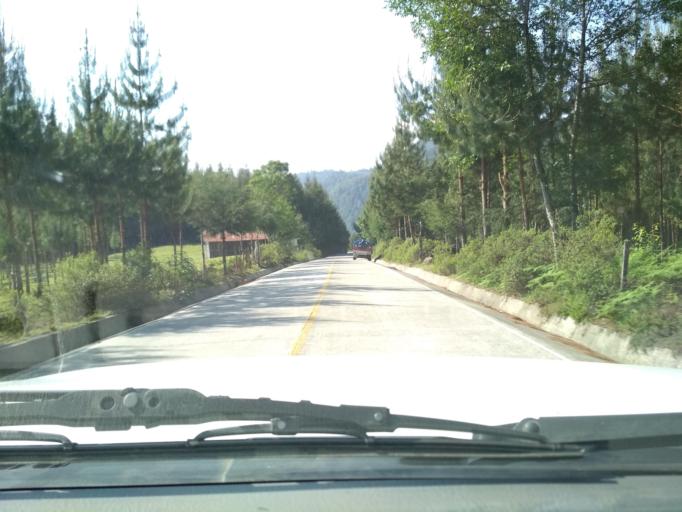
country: MX
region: Veracruz
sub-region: La Perla
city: Chilapa
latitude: 18.9951
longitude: -97.1860
